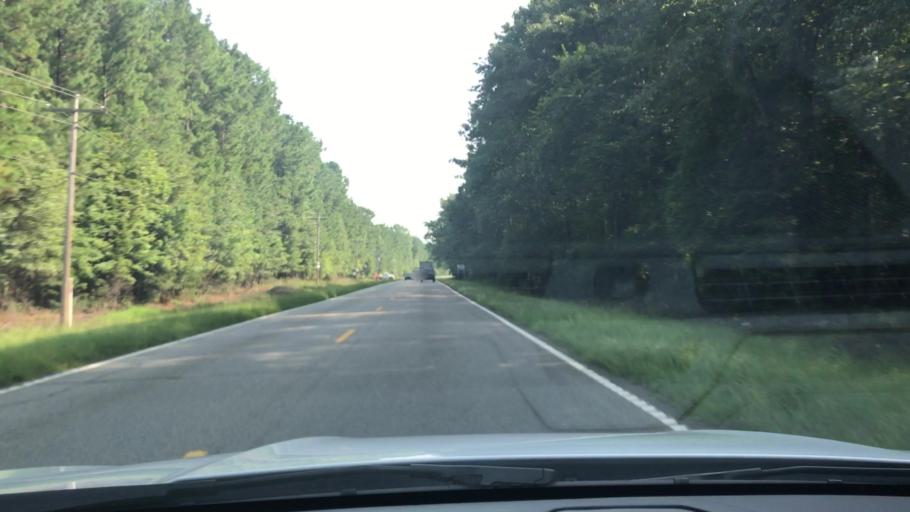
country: US
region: South Carolina
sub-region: Georgetown County
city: Georgetown
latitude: 33.4929
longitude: -79.2635
